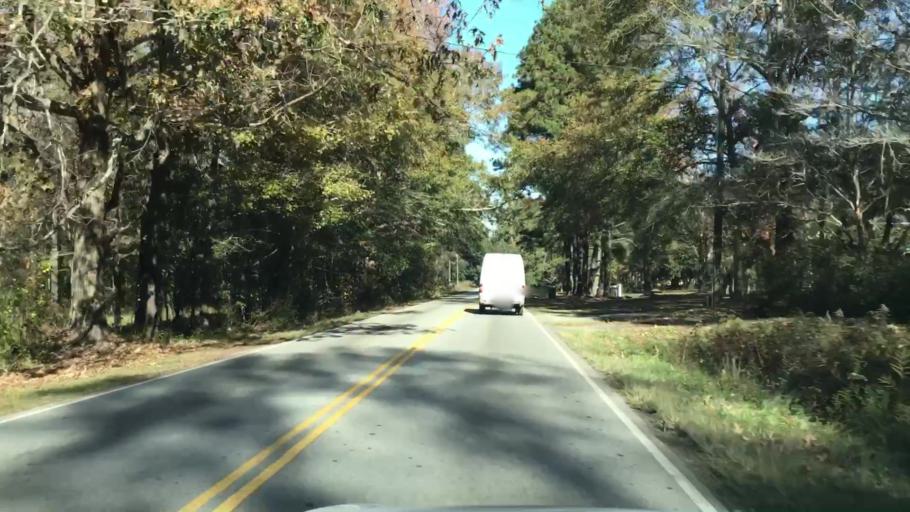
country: US
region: South Carolina
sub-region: Dorchester County
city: Summerville
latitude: 33.0173
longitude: -80.2398
